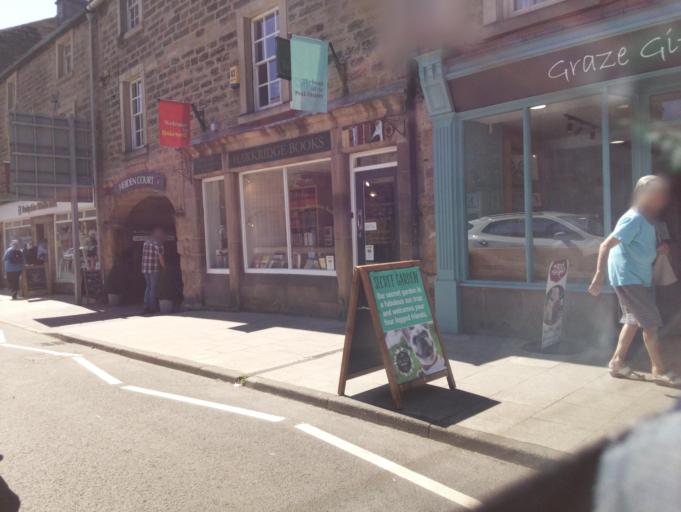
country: GB
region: England
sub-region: Derbyshire
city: Bakewell
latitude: 53.2126
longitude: -1.6753
